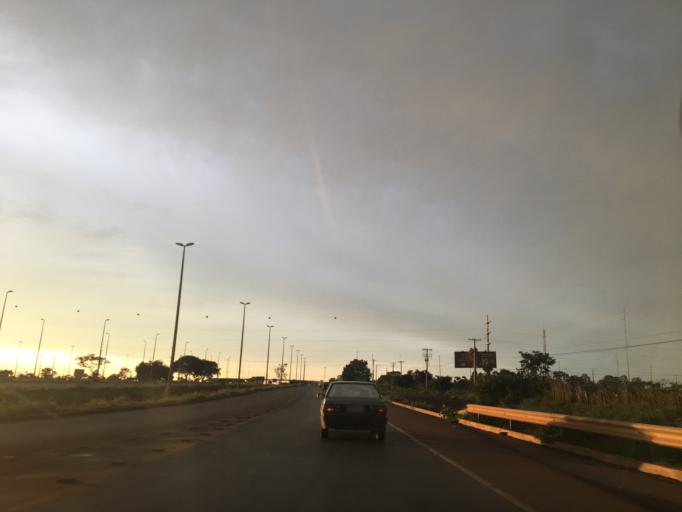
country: BR
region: Federal District
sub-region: Brasilia
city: Brasilia
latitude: -15.9743
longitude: -47.9910
